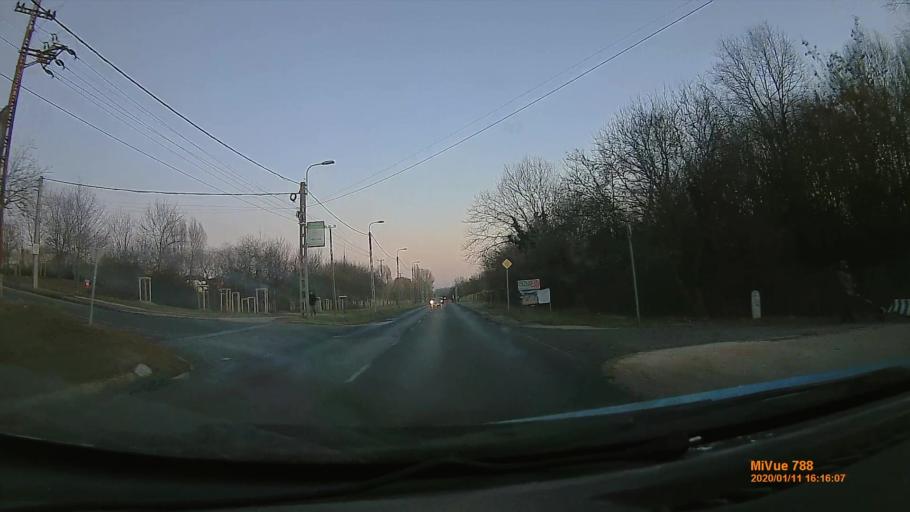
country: HU
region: Budapest
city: Budapest XVI. keruelet
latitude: 47.5279
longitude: 19.1976
